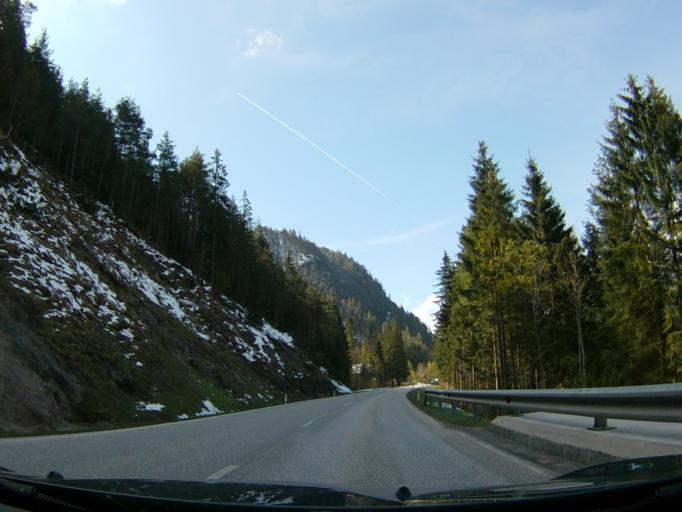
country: AT
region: Tyrol
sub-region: Politischer Bezirk Schwaz
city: Achenkirch
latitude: 47.4867
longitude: 11.7147
